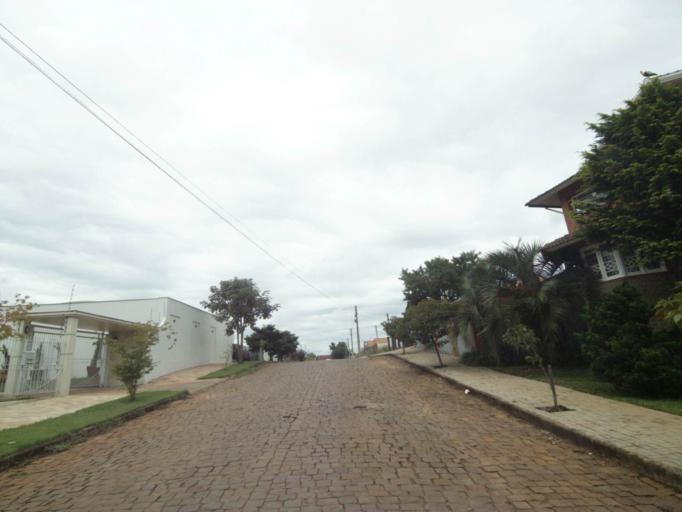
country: BR
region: Rio Grande do Sul
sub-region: Lagoa Vermelha
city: Lagoa Vermelha
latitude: -28.2169
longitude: -51.5321
